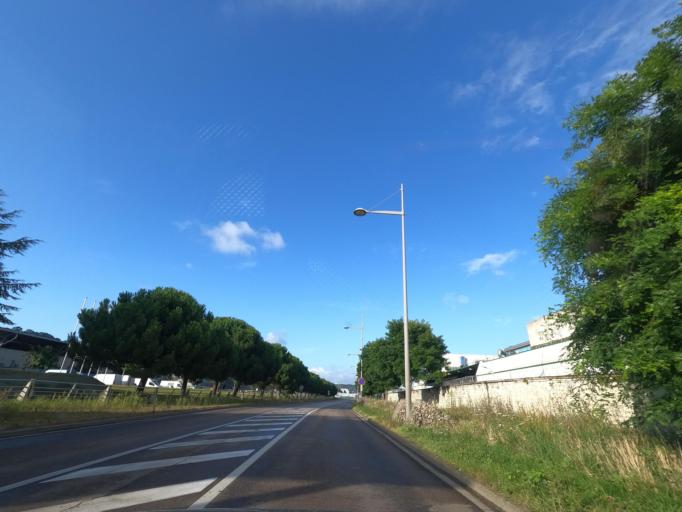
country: FR
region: Haute-Normandie
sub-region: Departement de la Seine-Maritime
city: Canteleu
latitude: 49.4273
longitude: 1.0311
